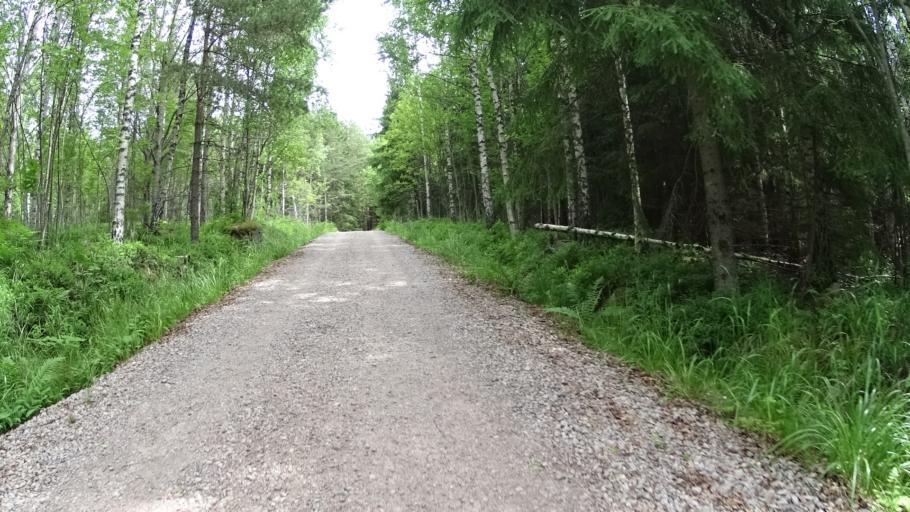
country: FI
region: Uusimaa
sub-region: Helsinki
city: Espoo
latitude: 60.2821
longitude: 24.5100
